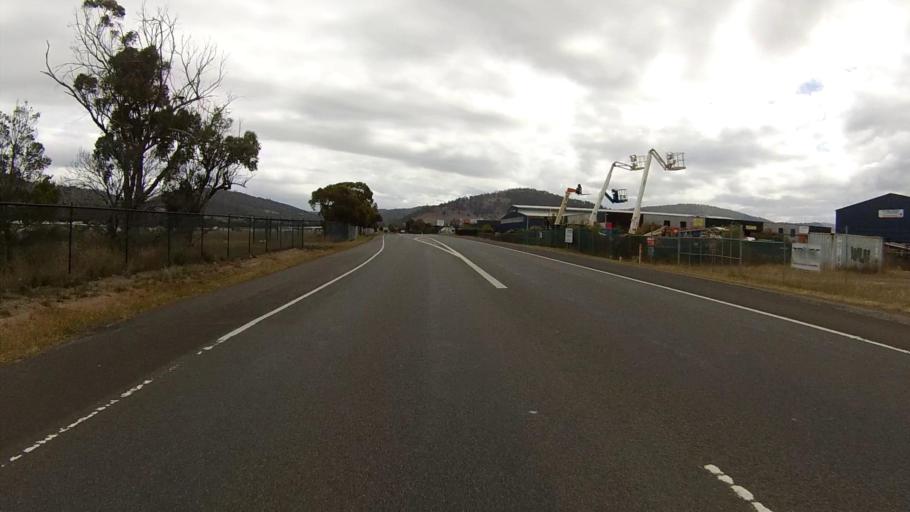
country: AU
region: Tasmania
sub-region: Clarence
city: Cambridge
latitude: -42.8301
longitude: 147.4716
